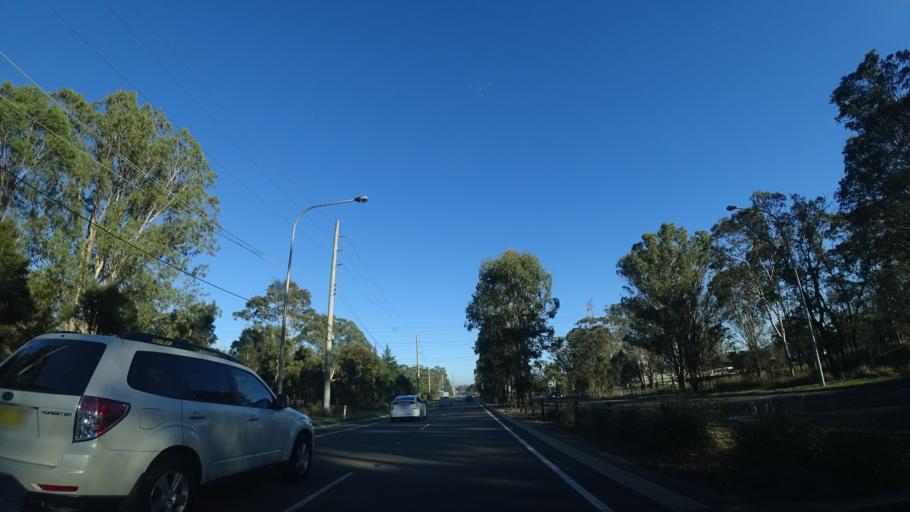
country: AU
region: New South Wales
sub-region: Blacktown
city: Riverstone
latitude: -33.6455
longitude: 150.8578
